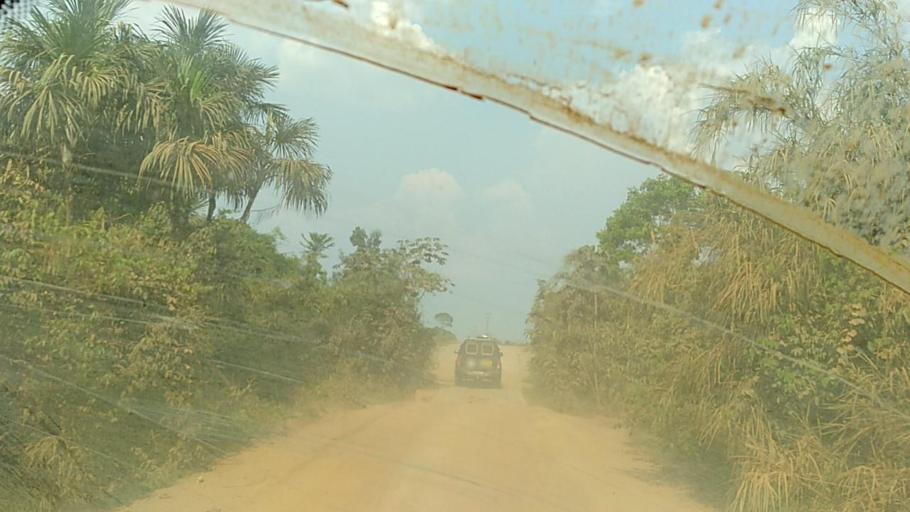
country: BR
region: Rondonia
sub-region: Porto Velho
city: Porto Velho
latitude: -8.6823
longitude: -63.2065
